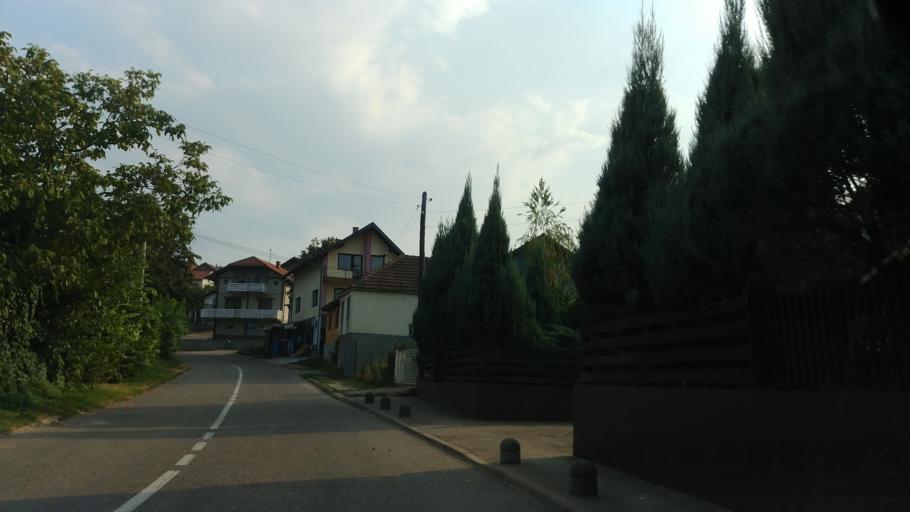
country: BA
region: Republika Srpska
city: Lopare
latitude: 44.7100
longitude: 18.8800
